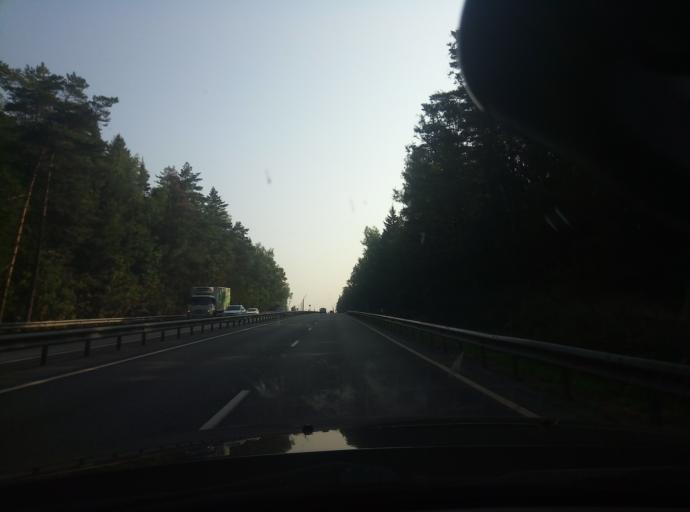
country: RU
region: Kaluga
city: Maloyaroslavets
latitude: 54.9723
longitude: 36.4821
